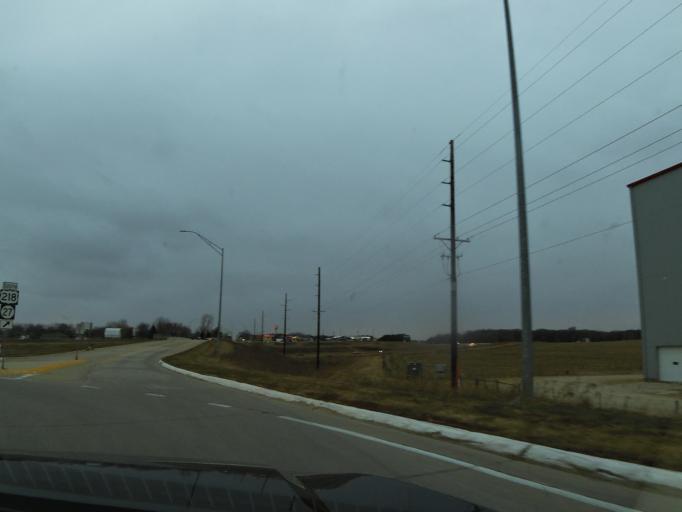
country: US
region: Iowa
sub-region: Bremer County
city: Waverly
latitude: 42.6496
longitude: -92.4490
